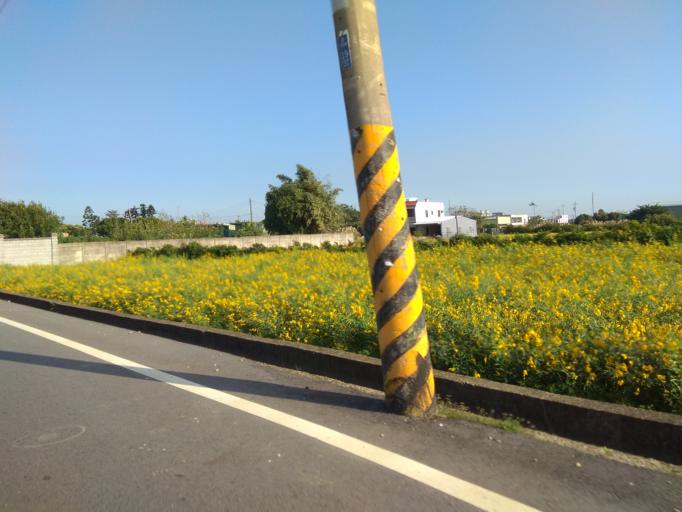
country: TW
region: Taiwan
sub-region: Hsinchu
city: Zhubei
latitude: 24.9813
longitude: 121.0798
